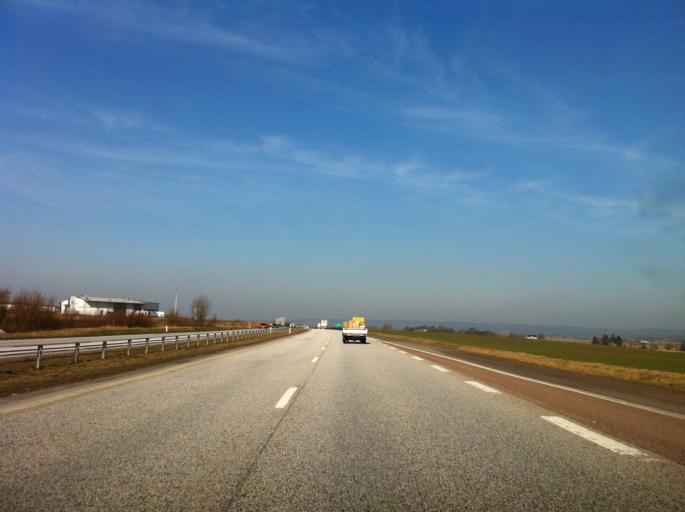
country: SE
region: Skane
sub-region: Angelholms Kommun
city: AEngelholm
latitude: 56.2571
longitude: 12.8973
